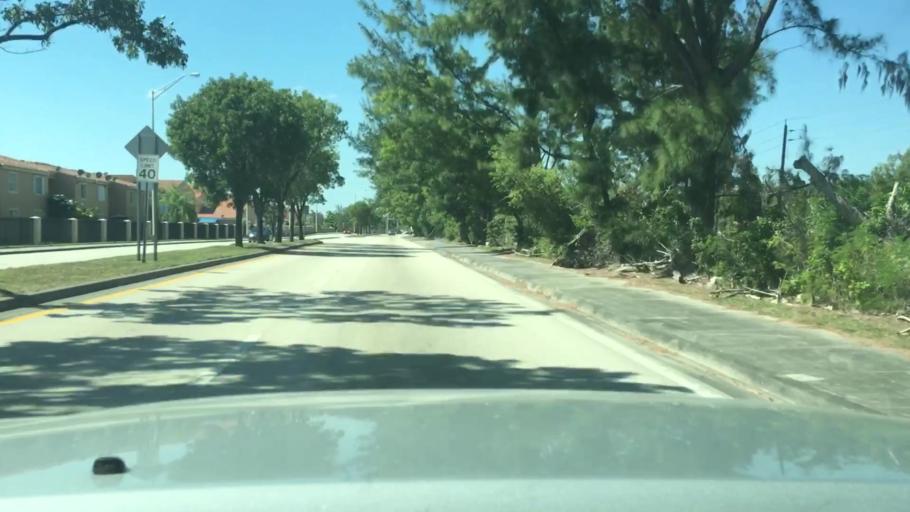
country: US
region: Florida
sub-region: Miami-Dade County
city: Tamiami
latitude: 25.7823
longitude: -80.3973
